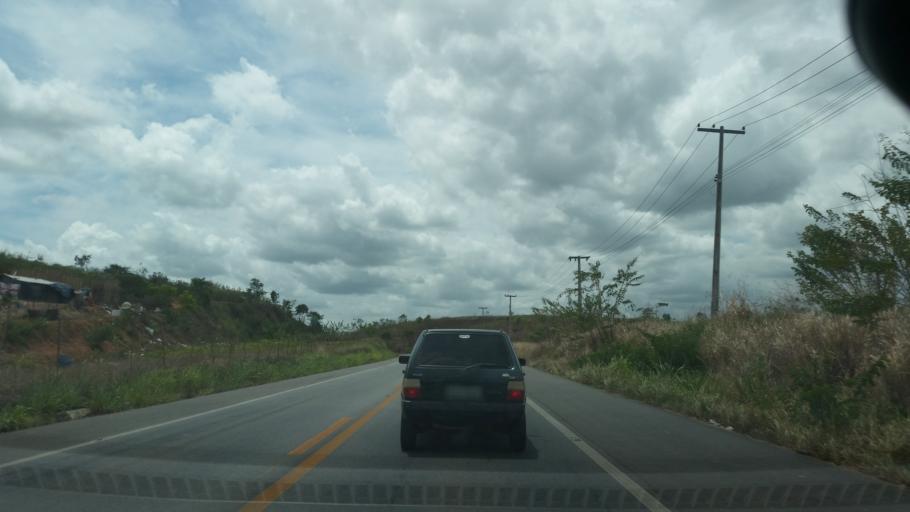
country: BR
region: Alagoas
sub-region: Uniao Dos Palmares
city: Uniao dos Palmares
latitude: -9.1791
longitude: -36.0341
